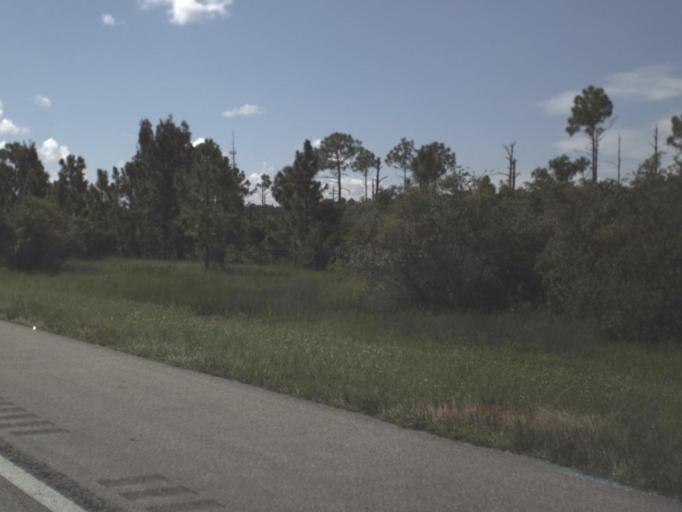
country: US
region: Florida
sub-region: Lee County
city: Burnt Store Marina
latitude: 26.8173
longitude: -81.9399
